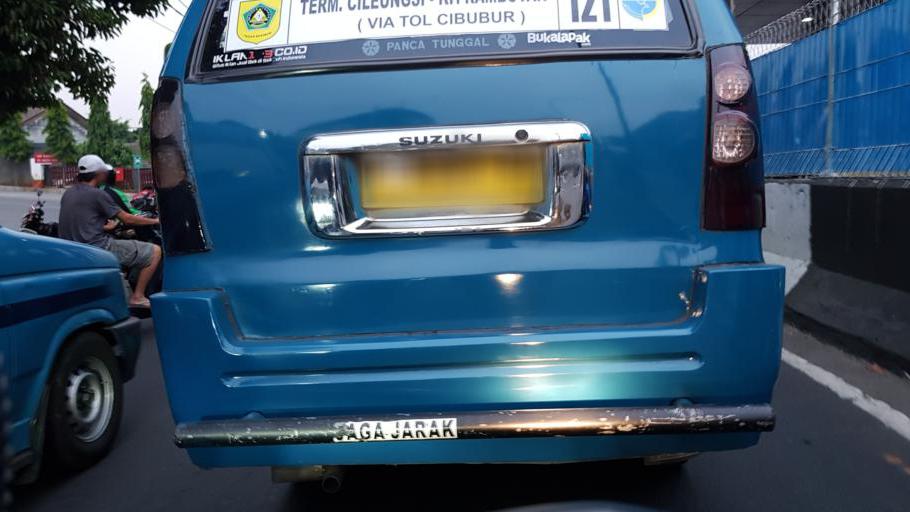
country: ID
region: Jakarta Raya
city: Jakarta
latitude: -6.3072
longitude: 106.8780
